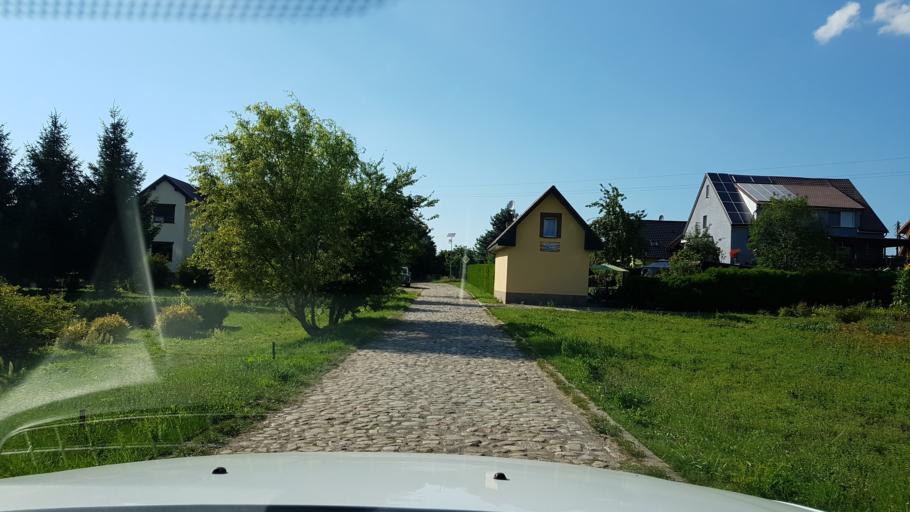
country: PL
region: West Pomeranian Voivodeship
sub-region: Powiat gryfinski
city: Banie
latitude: 53.0969
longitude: 14.6665
